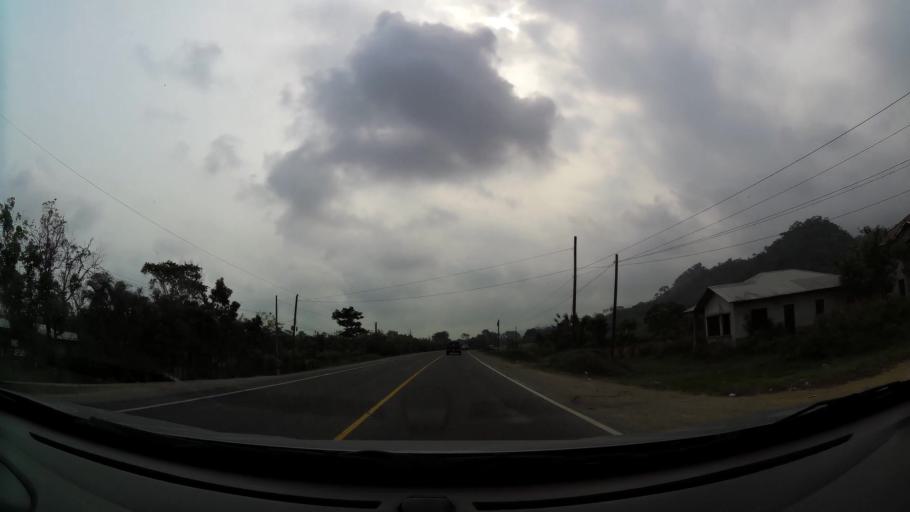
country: HN
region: Yoro
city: Guaimitas
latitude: 15.4923
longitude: -87.7498
